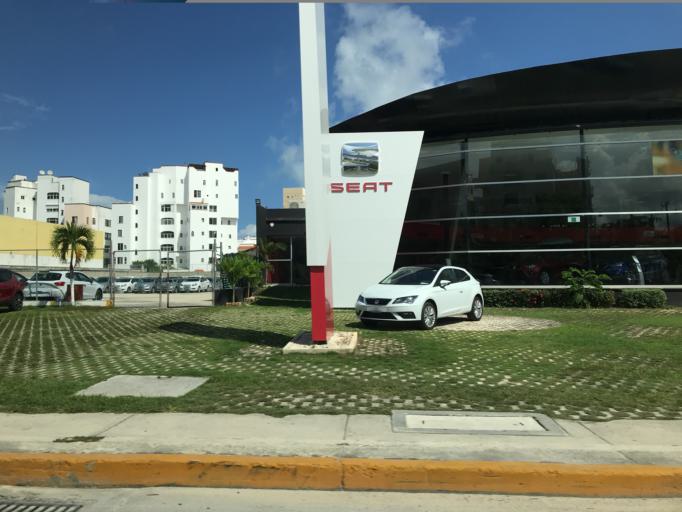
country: MX
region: Quintana Roo
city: Cancun
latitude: 21.1524
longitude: -86.8214
